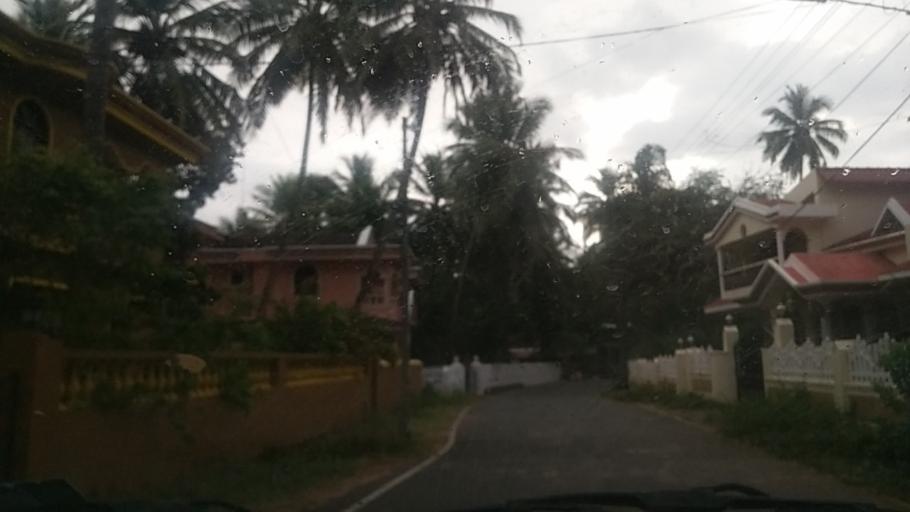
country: IN
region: Goa
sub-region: South Goa
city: Chinchinim
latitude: 15.1968
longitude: 73.9799
